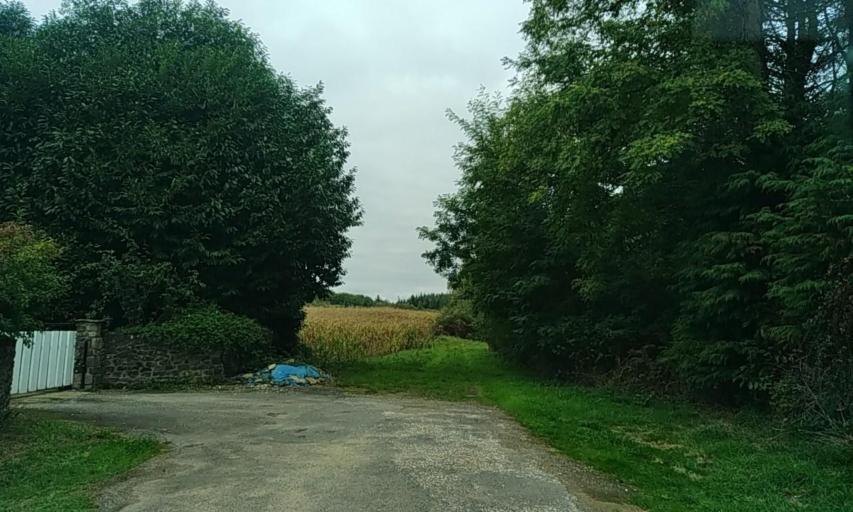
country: FR
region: Brittany
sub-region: Departement du Morbihan
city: Caudan
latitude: 47.8483
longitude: -3.3390
